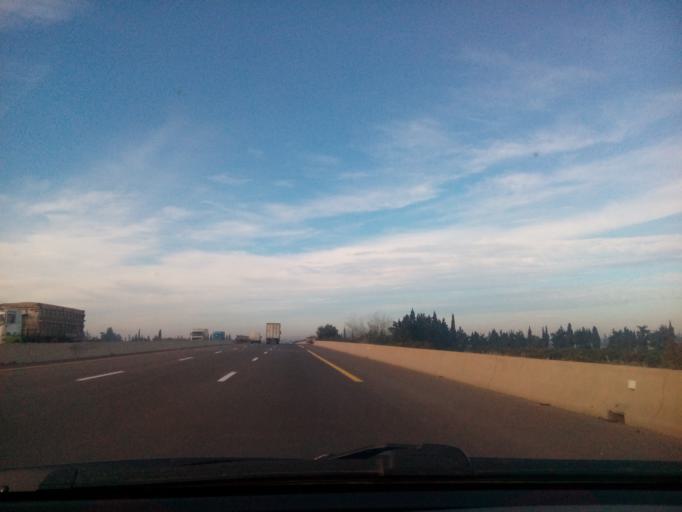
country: DZ
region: Mascara
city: Sig
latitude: 35.6172
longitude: 0.0249
